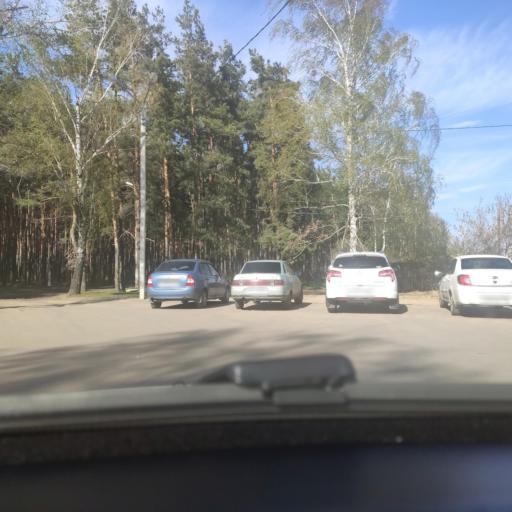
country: RU
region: Voronezj
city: Somovo
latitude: 51.7460
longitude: 39.3213
